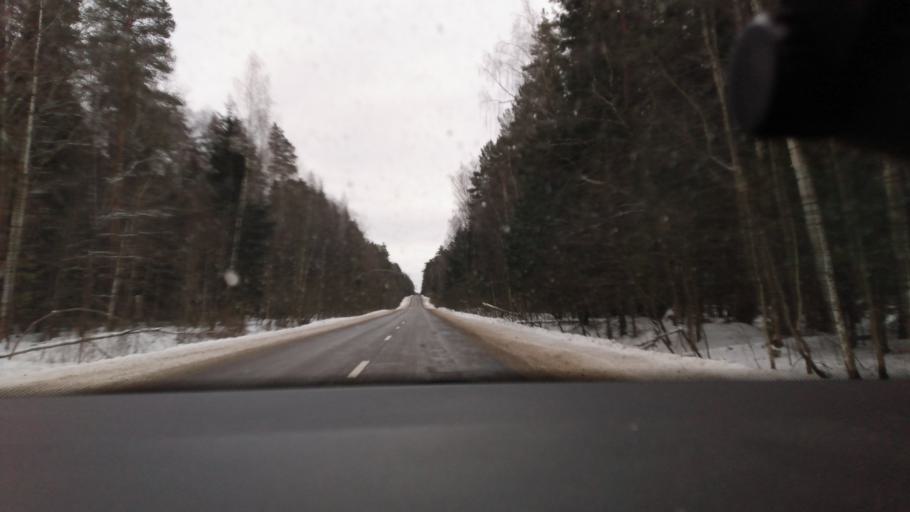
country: RU
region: Moskovskaya
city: Yegor'yevsk
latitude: 55.2211
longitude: 39.0763
